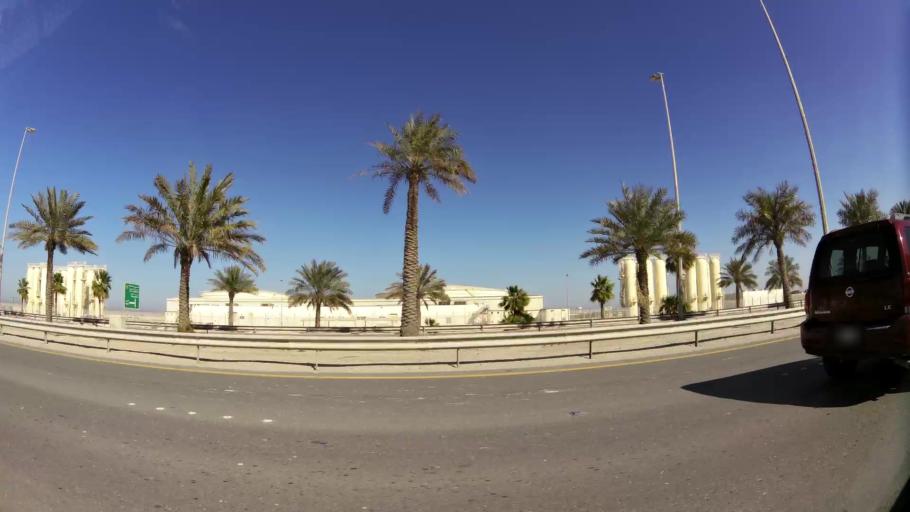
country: BH
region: Muharraq
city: Al Hadd
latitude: 26.2293
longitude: 50.6576
